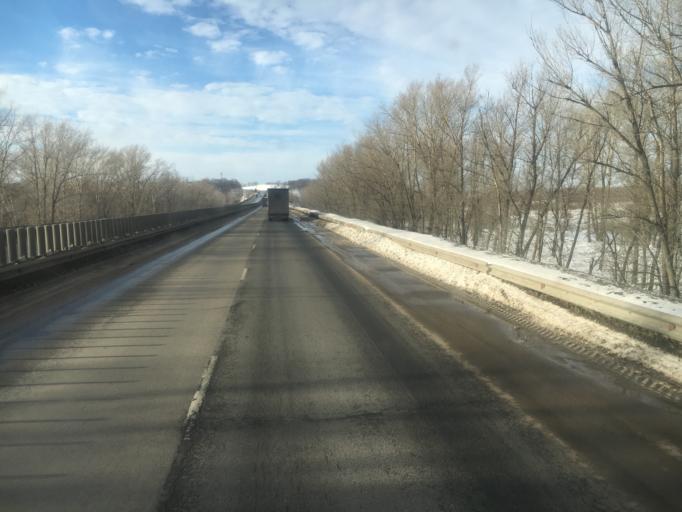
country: RU
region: Samara
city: Mirnyy
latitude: 53.4410
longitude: 50.2758
